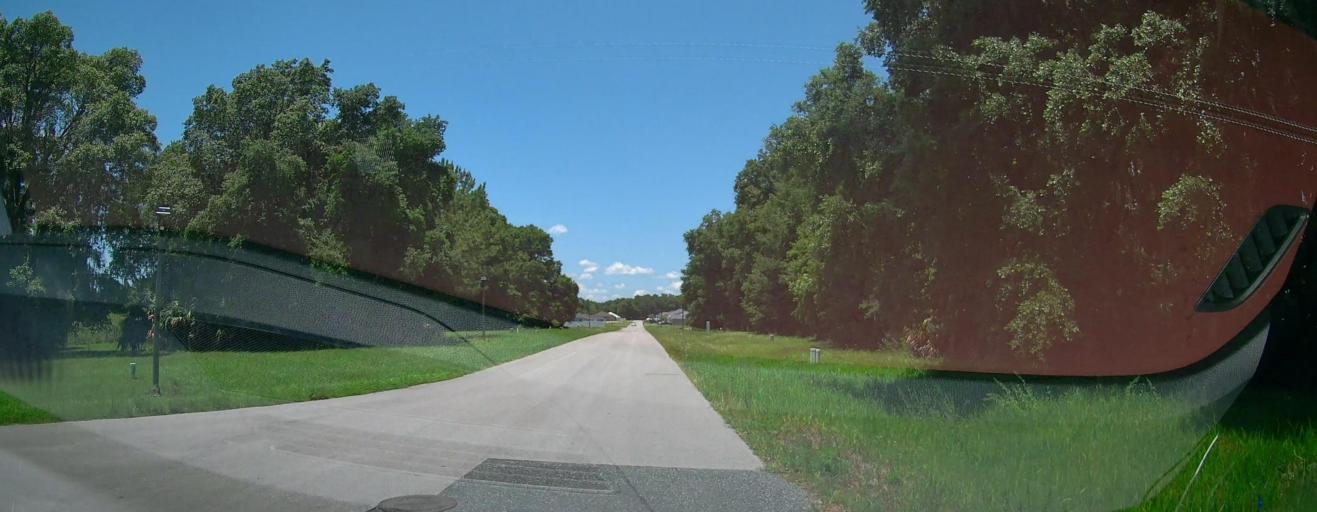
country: US
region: Florida
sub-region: Marion County
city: Belleview
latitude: 29.0930
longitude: -82.0717
